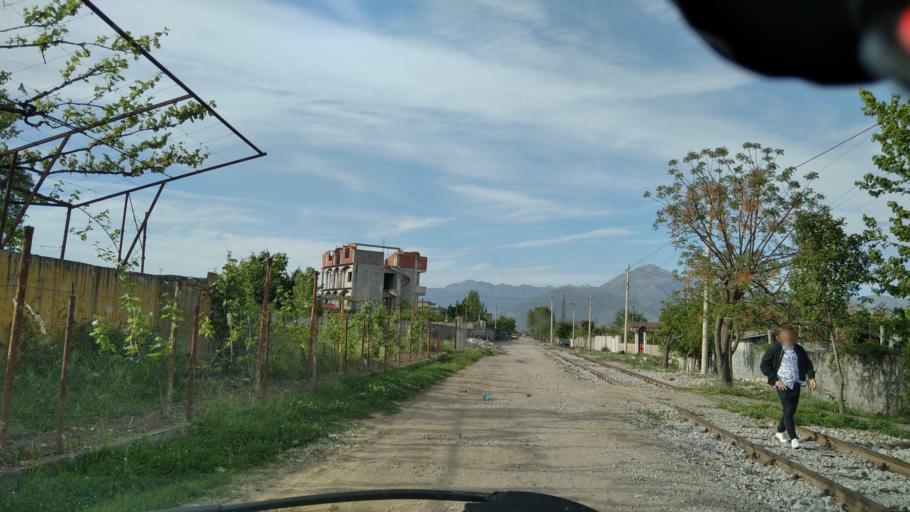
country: AL
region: Shkoder
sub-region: Rrethi i Shkodres
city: Shkoder
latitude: 42.0696
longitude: 19.5289
